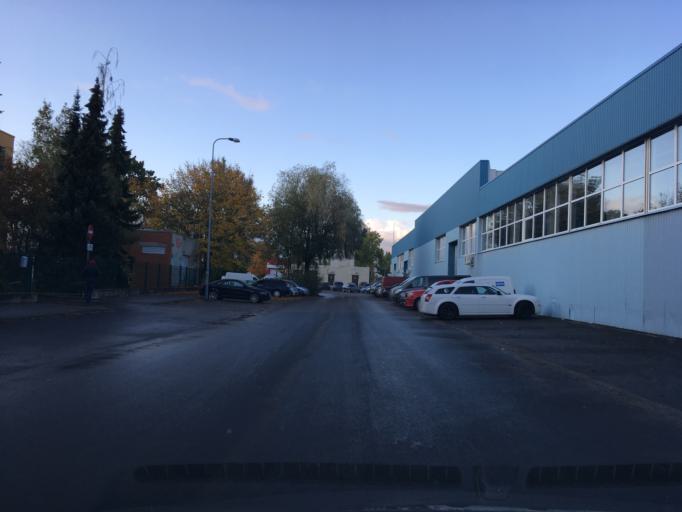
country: EE
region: Harju
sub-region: Tallinna linn
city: Tallinn
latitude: 59.4279
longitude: 24.8083
